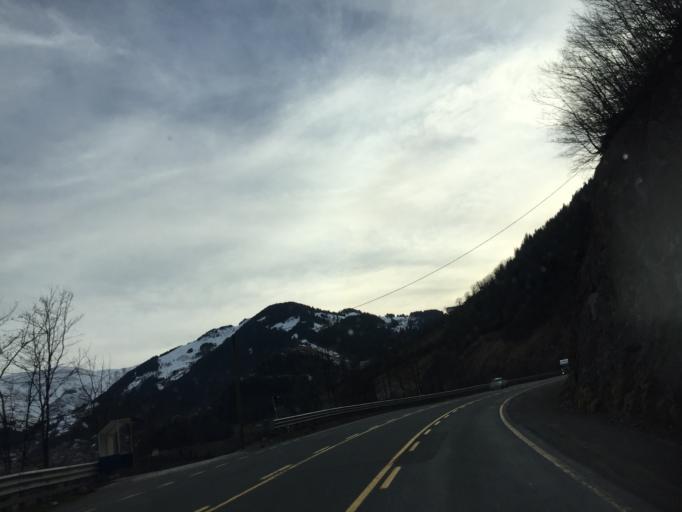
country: TR
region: Trabzon
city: Macka
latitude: 40.7037
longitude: 39.4892
